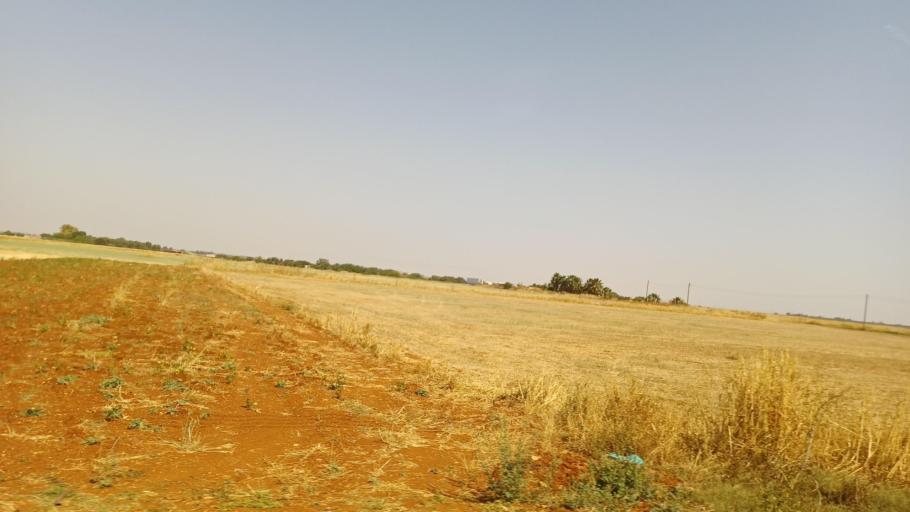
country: CY
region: Ammochostos
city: Avgorou
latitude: 35.0560
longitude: 33.8558
